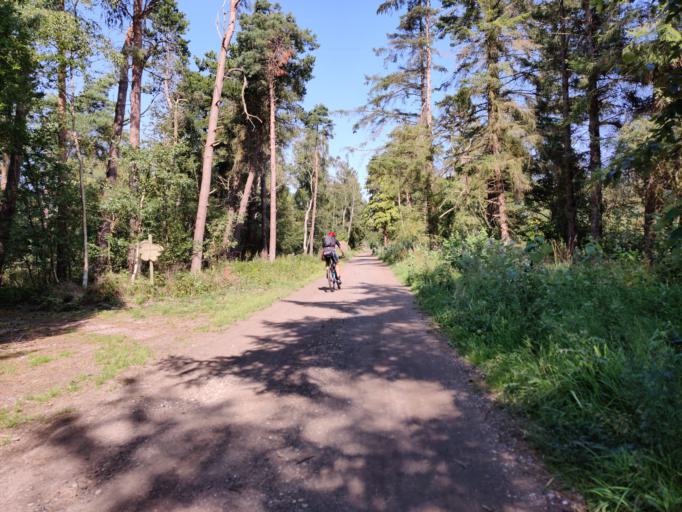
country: DK
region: Zealand
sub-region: Guldborgsund Kommune
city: Nykobing Falster
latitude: 54.6067
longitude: 11.9522
